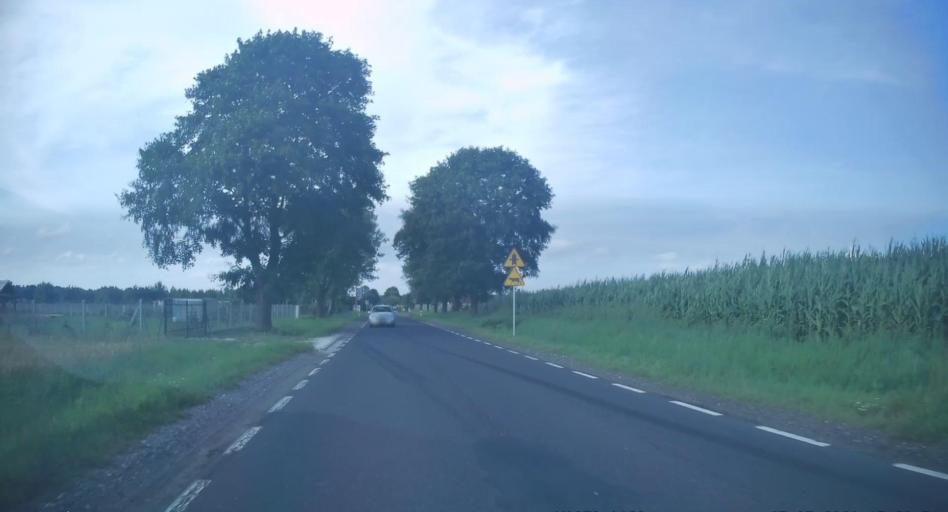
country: PL
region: Lodz Voivodeship
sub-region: Powiat tomaszowski
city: Rzeczyca
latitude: 51.6710
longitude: 20.2644
